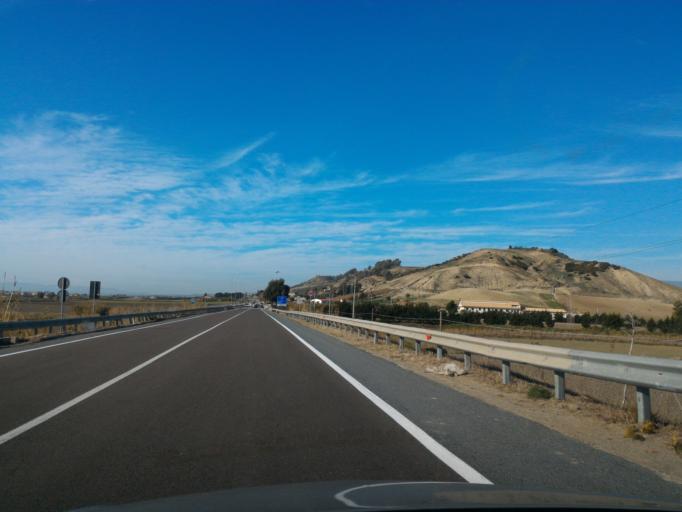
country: IT
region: Calabria
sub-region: Provincia di Crotone
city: Le Castella
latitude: 38.9470
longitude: 16.9487
